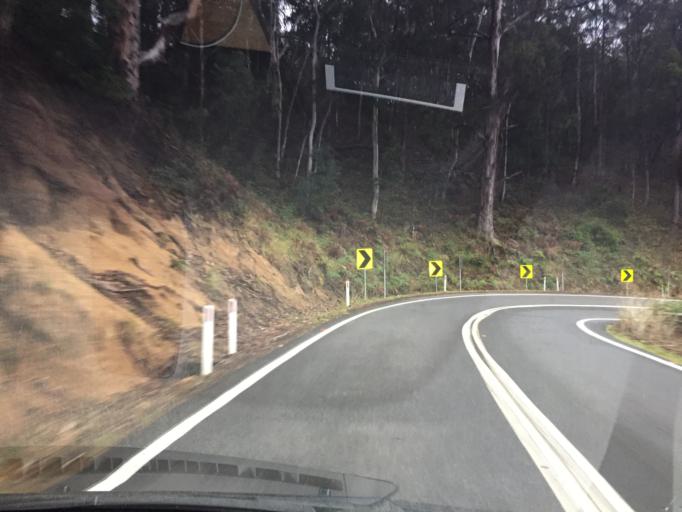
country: AU
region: New South Wales
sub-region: Bega Valley
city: Bega
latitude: -36.6120
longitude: 149.4773
